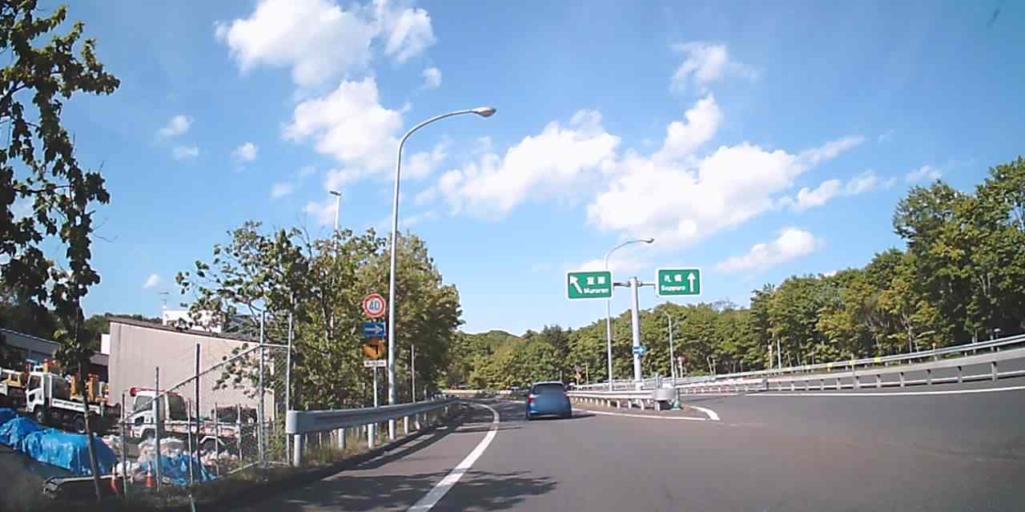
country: JP
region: Hokkaido
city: Tomakomai
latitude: 42.6314
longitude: 141.4902
